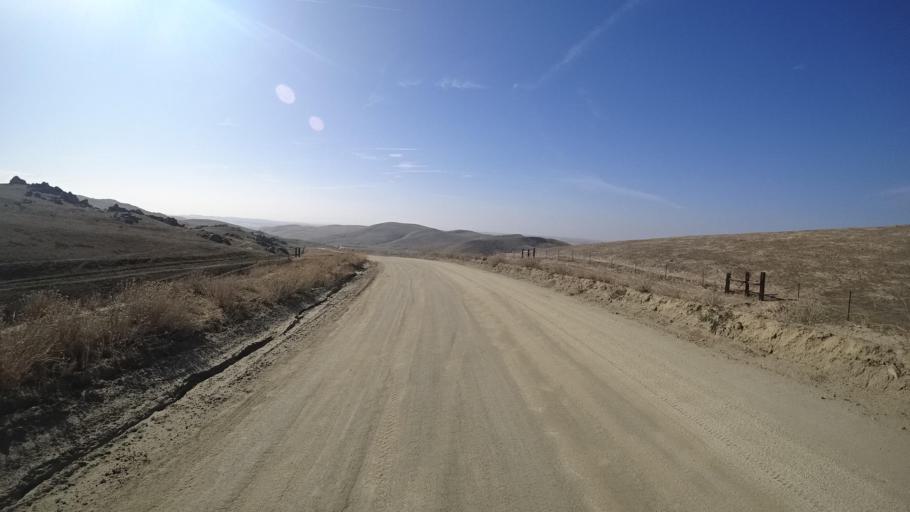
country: US
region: California
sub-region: Kern County
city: Oildale
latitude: 35.4804
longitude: -118.8248
